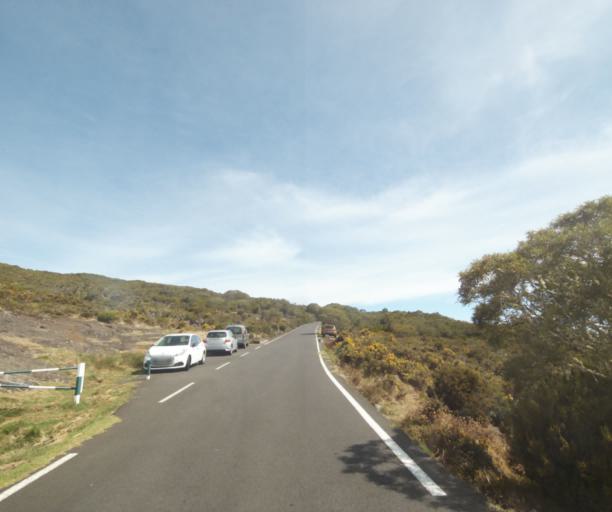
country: RE
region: Reunion
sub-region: Reunion
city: Trois-Bassins
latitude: -21.0627
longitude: 55.3786
